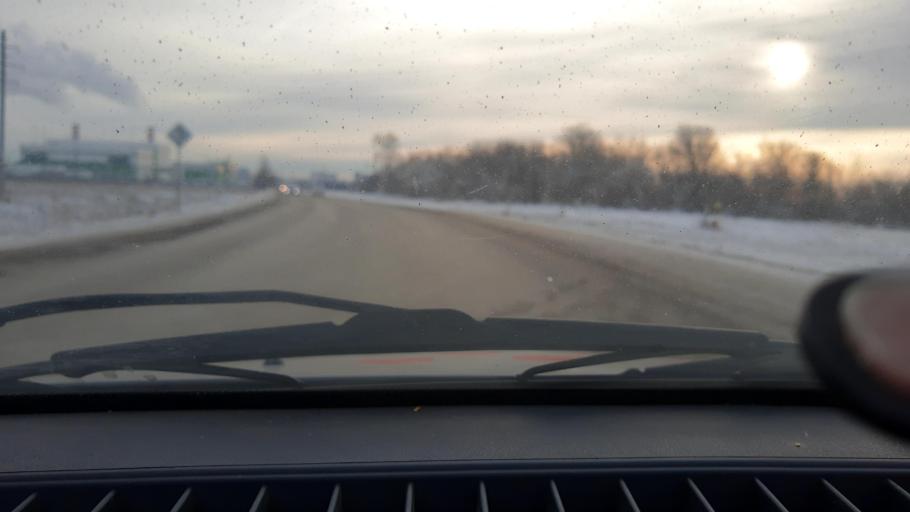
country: RU
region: Bashkortostan
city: Mikhaylovka
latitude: 54.8046
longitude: 55.8244
